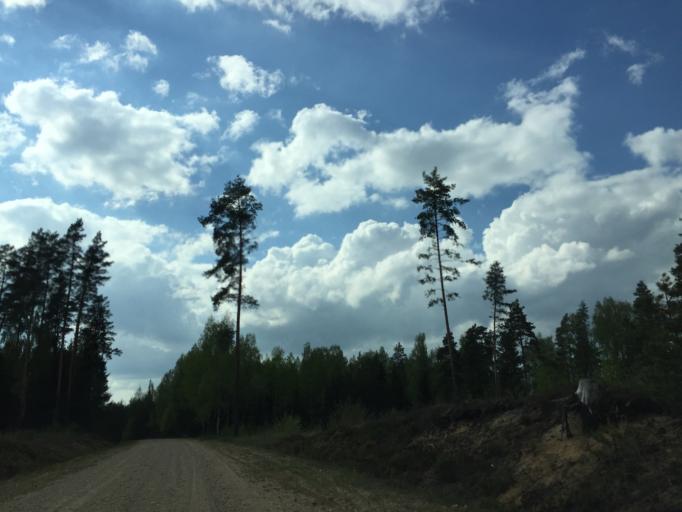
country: LV
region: Sigulda
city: Sigulda
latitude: 57.2956
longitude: 24.8361
